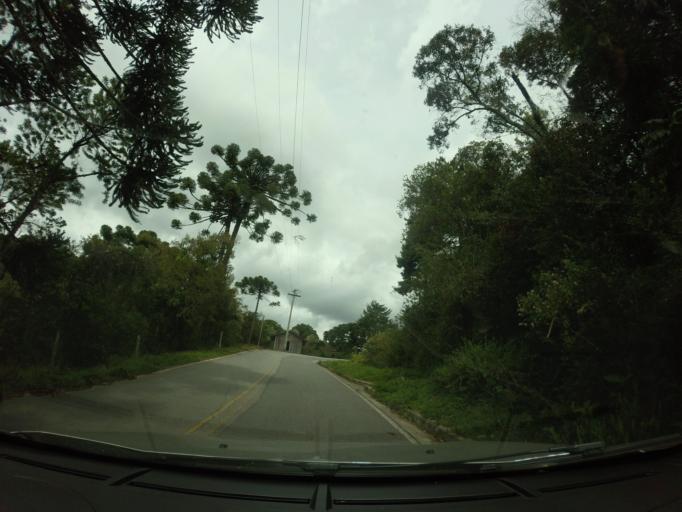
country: BR
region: Sao Paulo
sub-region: Campos Do Jordao
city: Campos do Jordao
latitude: -22.6747
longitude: -45.5901
